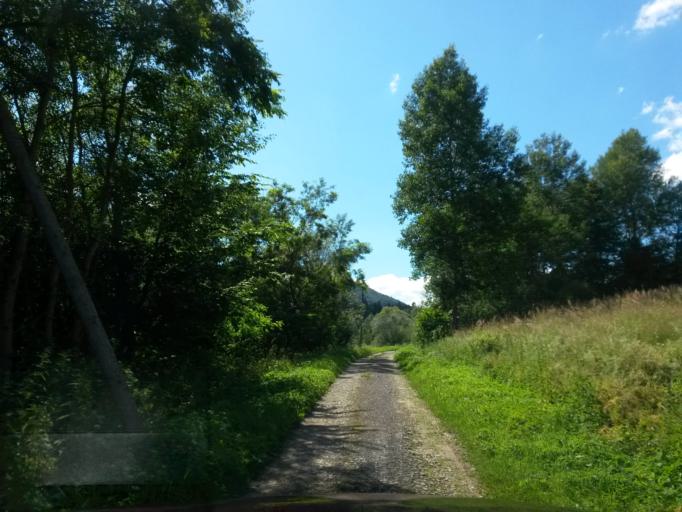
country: SK
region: Kosicky
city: Medzev
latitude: 48.7941
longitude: 20.7546
